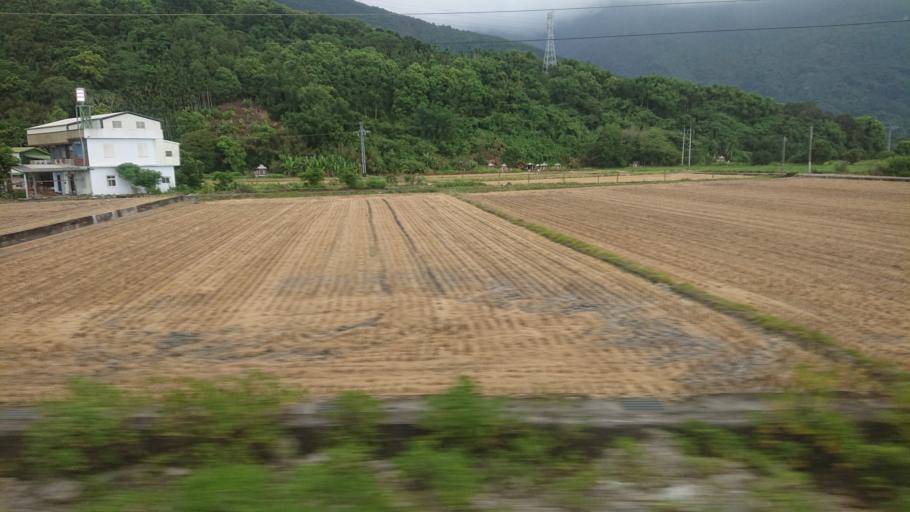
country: TW
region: Taiwan
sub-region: Hualien
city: Hualian
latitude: 23.7330
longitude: 121.4400
